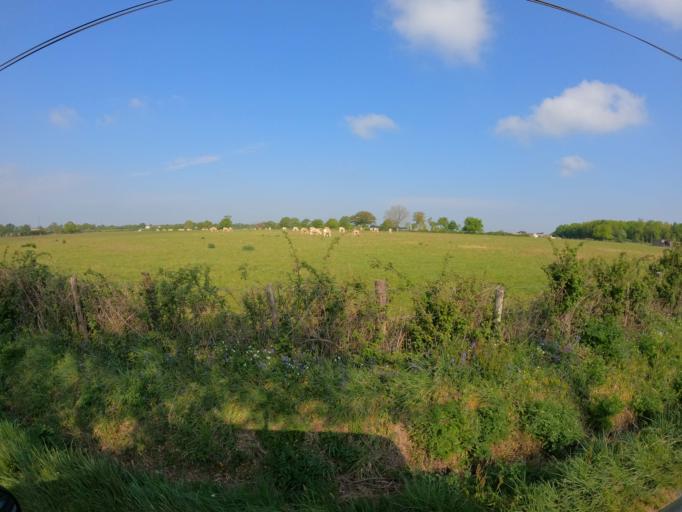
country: FR
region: Pays de la Loire
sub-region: Departement de Maine-et-Loire
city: Torfou
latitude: 47.0557
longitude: -1.0927
